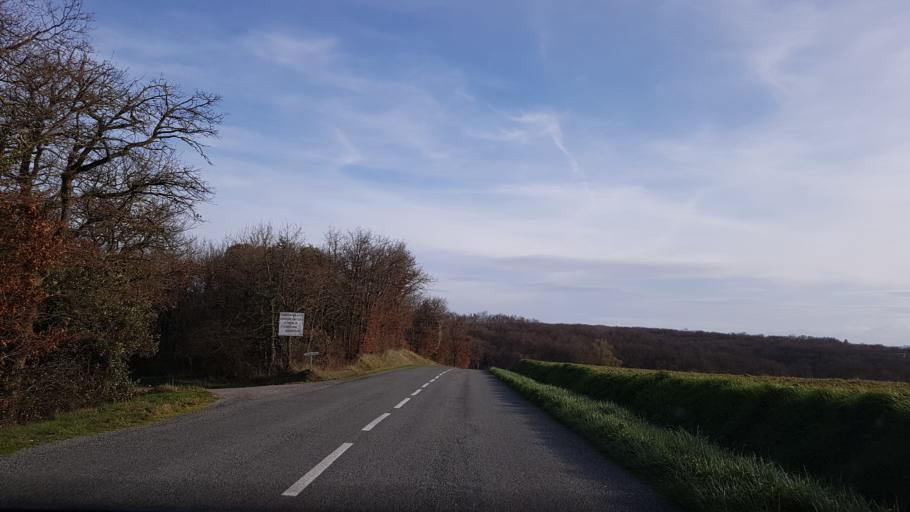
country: FR
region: Languedoc-Roussillon
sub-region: Departement de l'Aude
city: Villeneuve-la-Comptal
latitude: 43.2244
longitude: 1.9177
